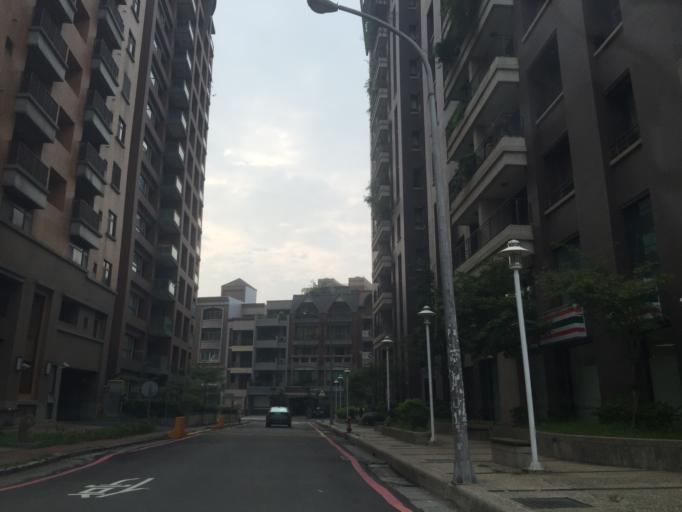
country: TW
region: Taiwan
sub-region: Hsinchu
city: Zhubei
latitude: 24.8329
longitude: 121.0188
